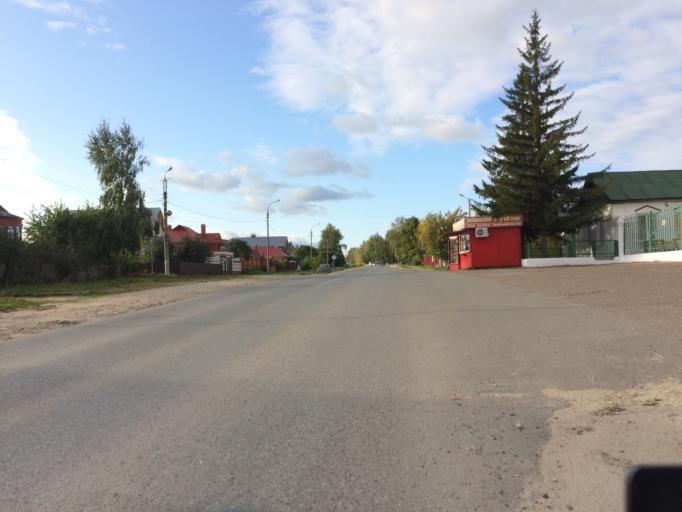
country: RU
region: Mariy-El
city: Yoshkar-Ola
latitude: 56.6503
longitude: 47.9803
